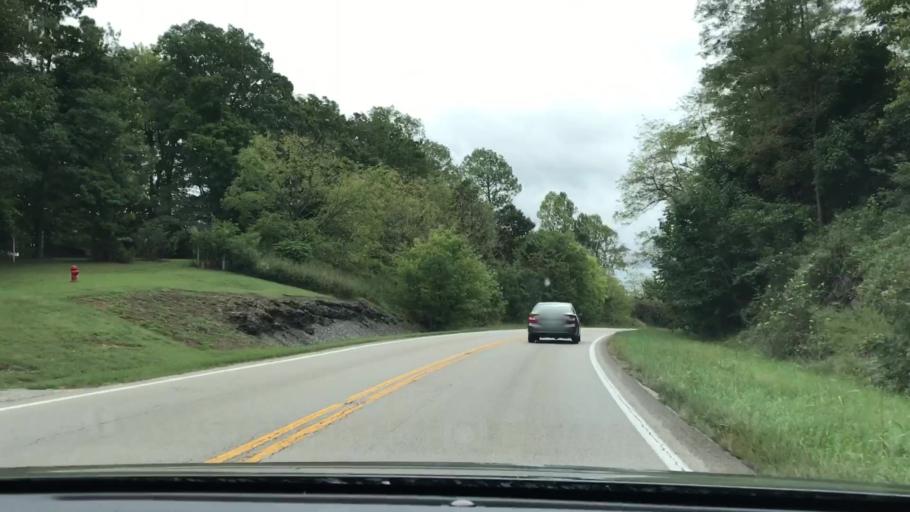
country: US
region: Kentucky
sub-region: Metcalfe County
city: Edmonton
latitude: 36.9055
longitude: -85.7552
